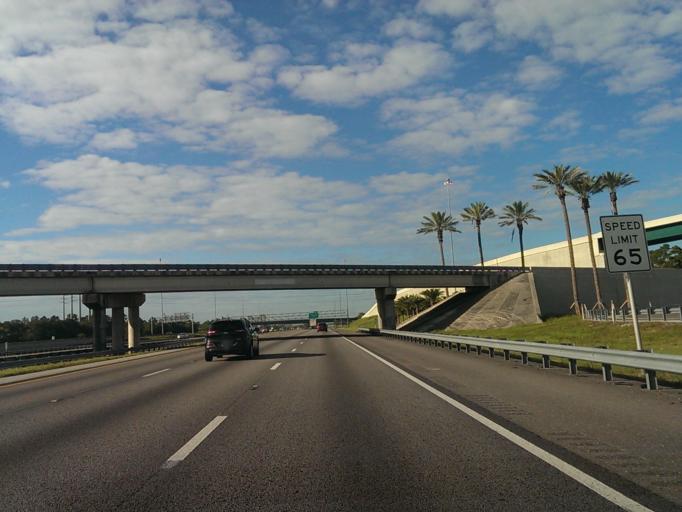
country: US
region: Florida
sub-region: Osceola County
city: Celebration
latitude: 28.3317
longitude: -81.5466
